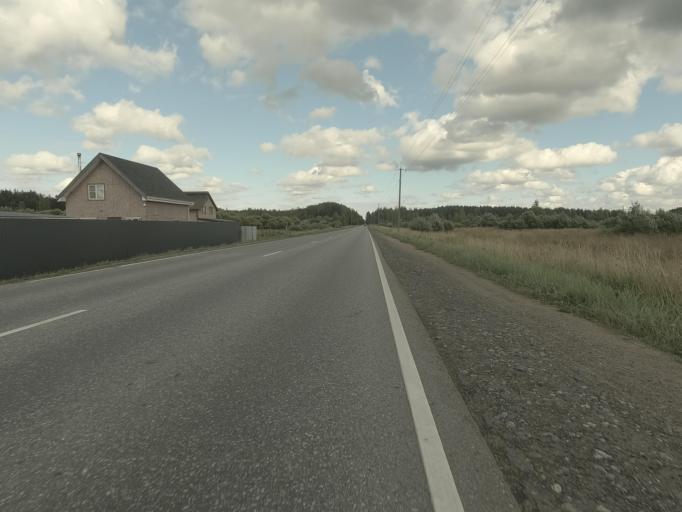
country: RU
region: Leningrad
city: Shcheglovo
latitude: 60.0289
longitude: 30.7863
